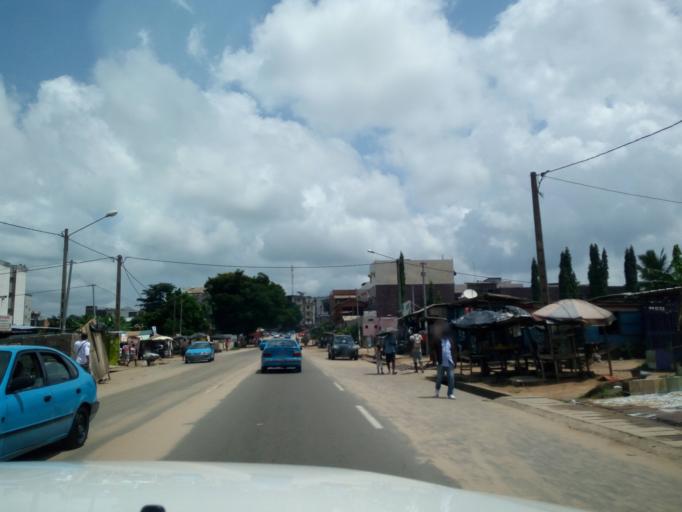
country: CI
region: Lagunes
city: Abidjan
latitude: 5.3395
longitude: -4.0947
